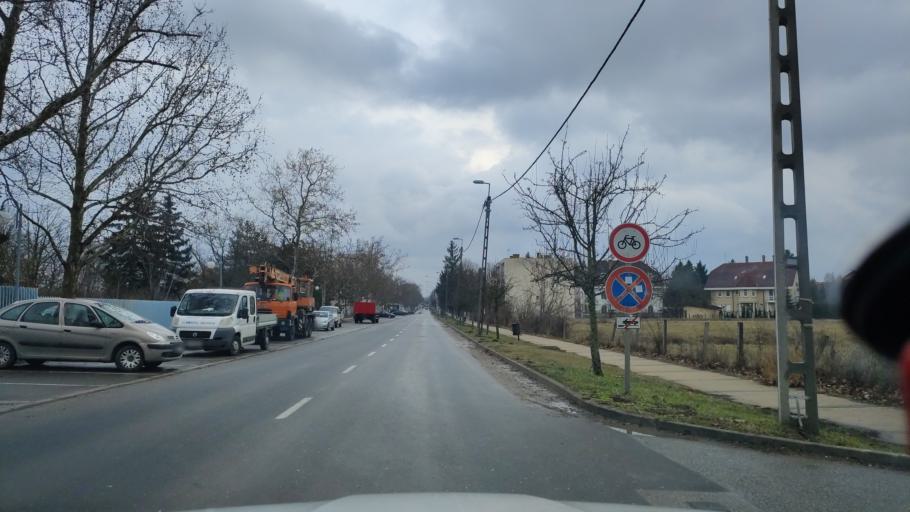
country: HU
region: Hajdu-Bihar
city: Hajduszoboszlo
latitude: 47.4527
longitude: 21.3943
